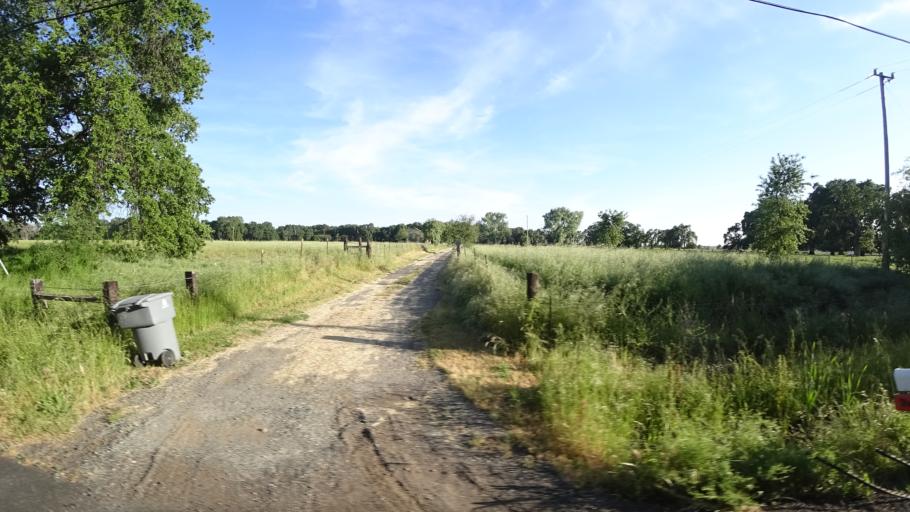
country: US
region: California
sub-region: Placer County
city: Lincoln
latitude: 38.9265
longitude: -121.2793
